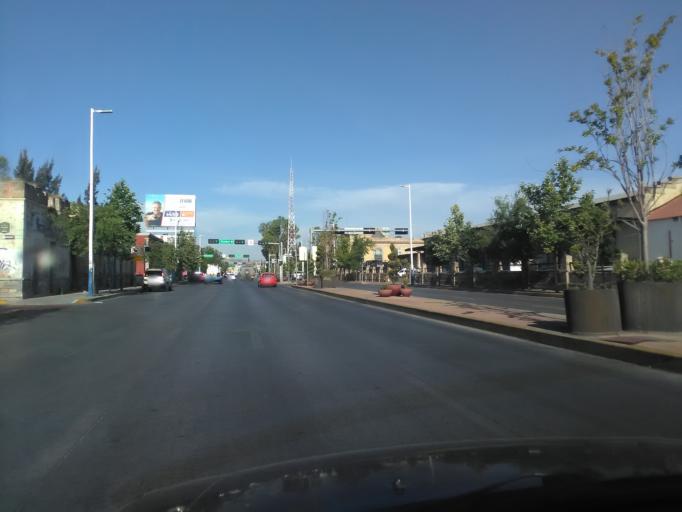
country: MX
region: Durango
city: Victoria de Durango
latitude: 24.0348
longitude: -104.6705
